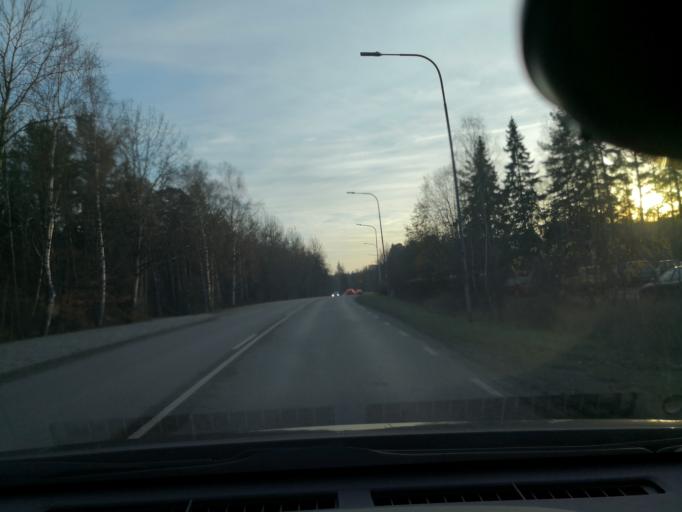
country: SE
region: Vaestmanland
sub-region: Vasteras
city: Vasteras
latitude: 59.6145
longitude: 16.5058
